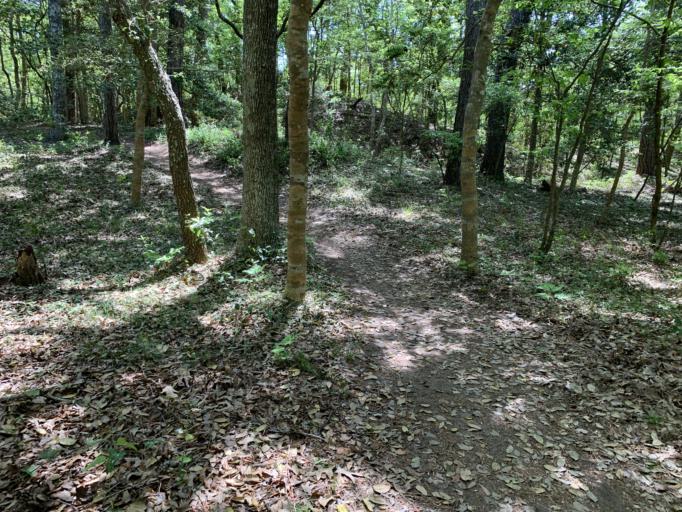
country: US
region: North Carolina
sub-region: Dare County
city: Kill Devil Hills
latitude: 35.9874
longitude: -75.6645
